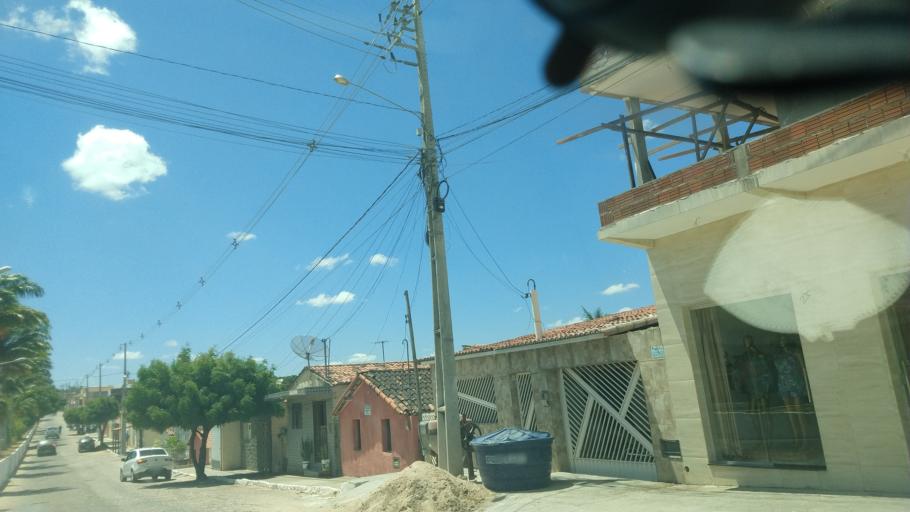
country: BR
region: Rio Grande do Norte
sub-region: Cerro Cora
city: Cerro Cora
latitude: -6.0475
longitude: -36.3498
